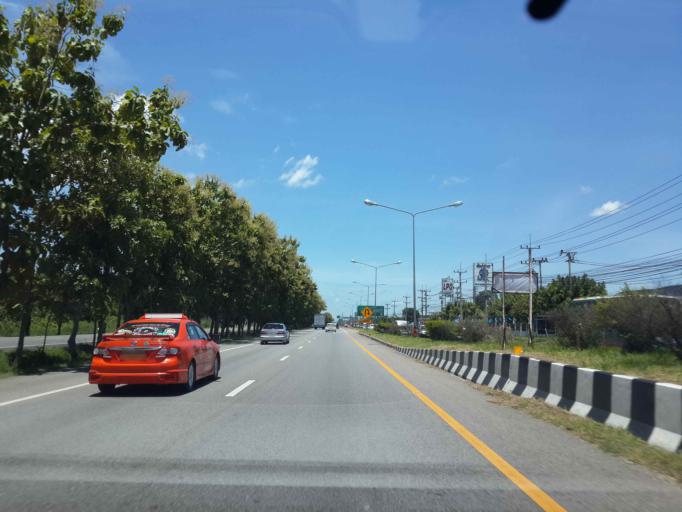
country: TH
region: Phetchaburi
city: Khao Yoi
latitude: 13.3061
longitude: 99.8250
